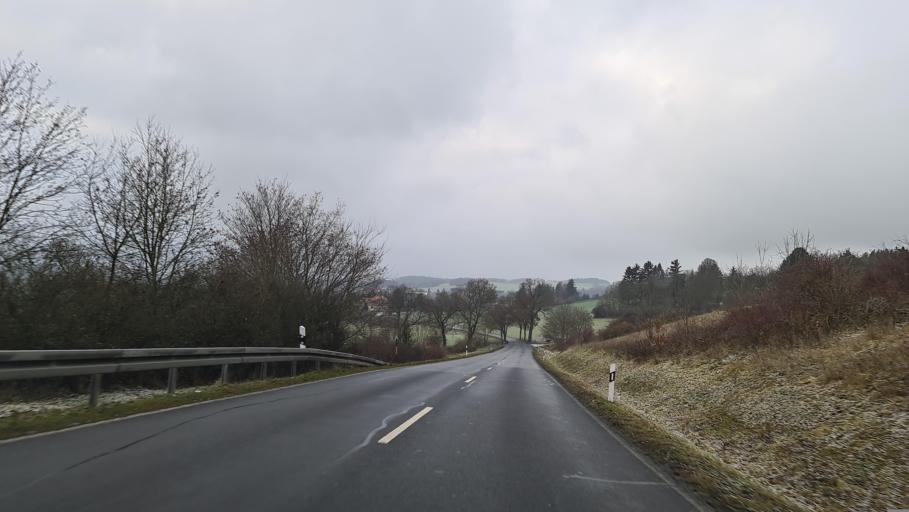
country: DE
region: Saxony
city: Weischlitz
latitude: 50.4590
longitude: 12.0659
